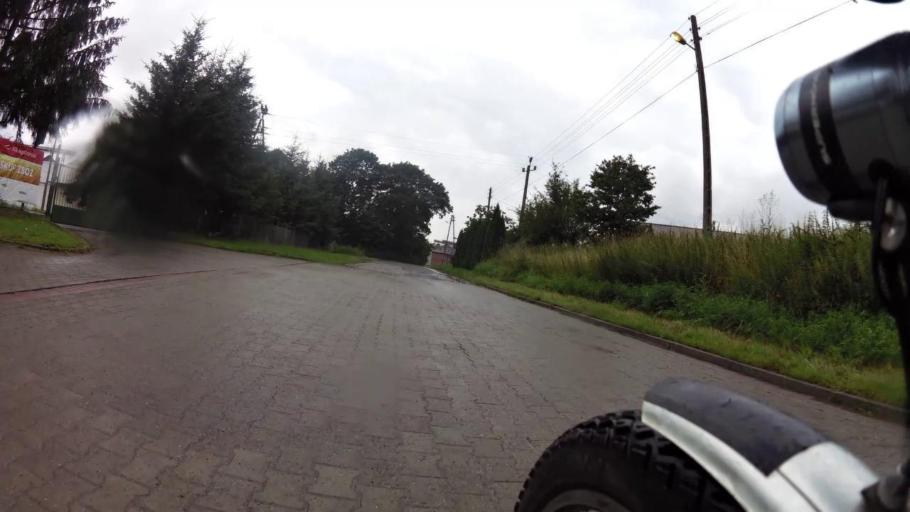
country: PL
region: West Pomeranian Voivodeship
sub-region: Powiat gryfinski
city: Banie
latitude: 53.1021
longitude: 14.6499
